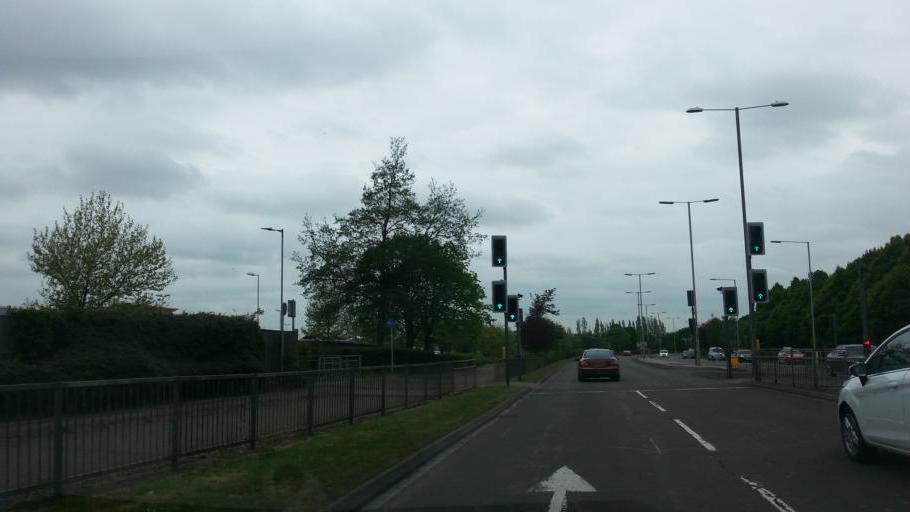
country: GB
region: England
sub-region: Peterborough
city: Peterborough
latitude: 52.5944
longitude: -0.2592
